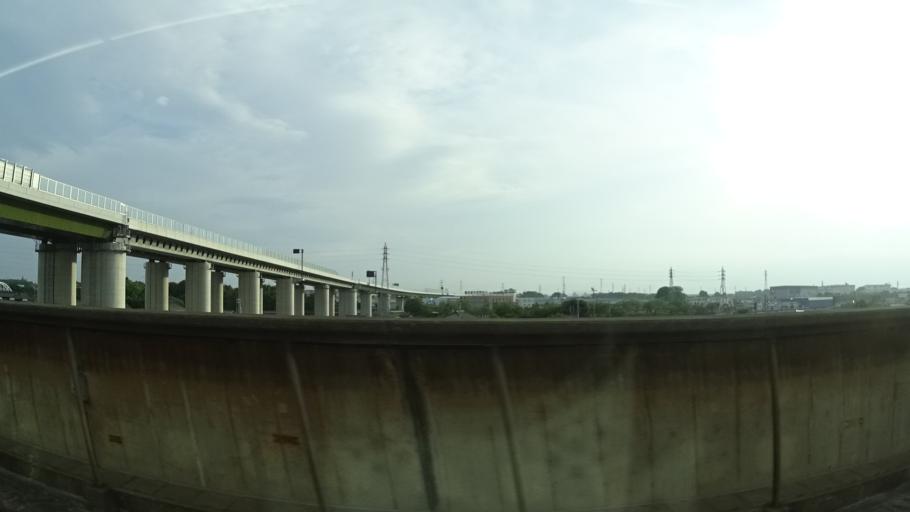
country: JP
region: Saitama
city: Okegawa
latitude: 36.0313
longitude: 139.5781
